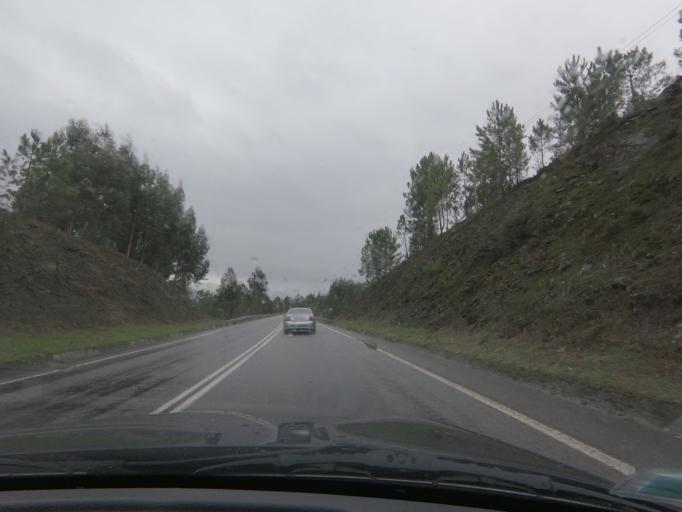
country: PT
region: Porto
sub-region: Amarante
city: Amarante
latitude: 41.3289
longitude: -8.0406
